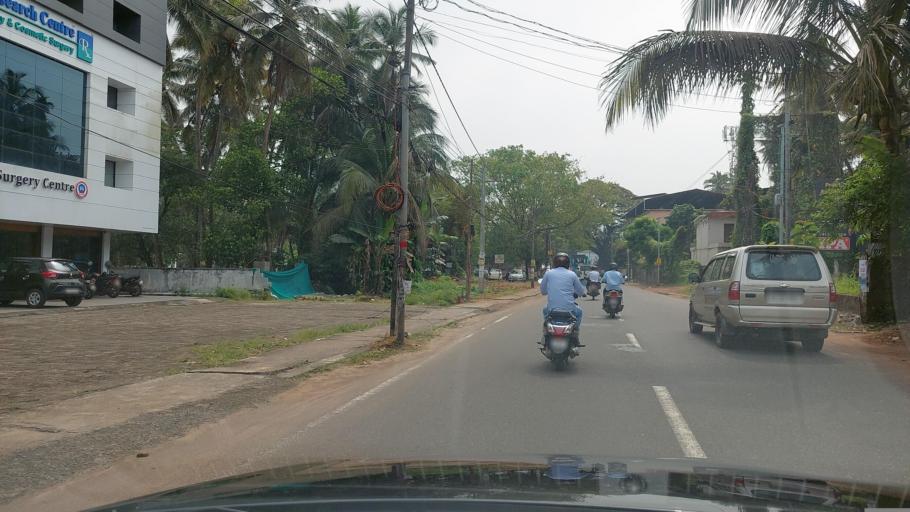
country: IN
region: Kerala
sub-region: Kozhikode
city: Kozhikode
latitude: 11.2699
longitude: 75.7778
